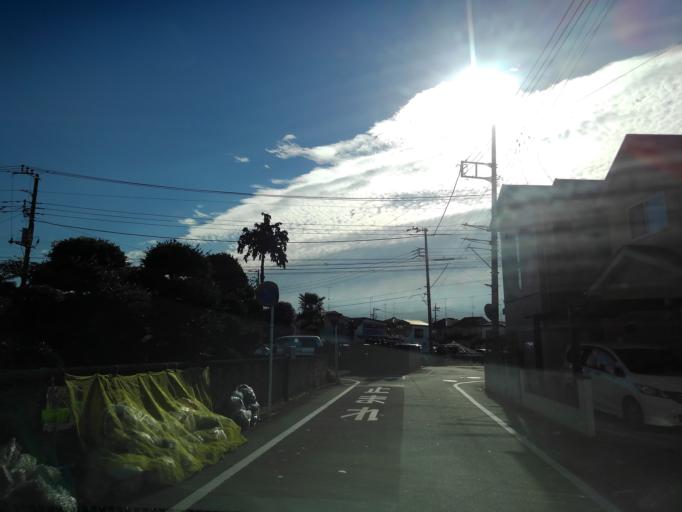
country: JP
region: Tokyo
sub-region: Machida-shi
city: Machida
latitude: 35.5815
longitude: 139.3967
